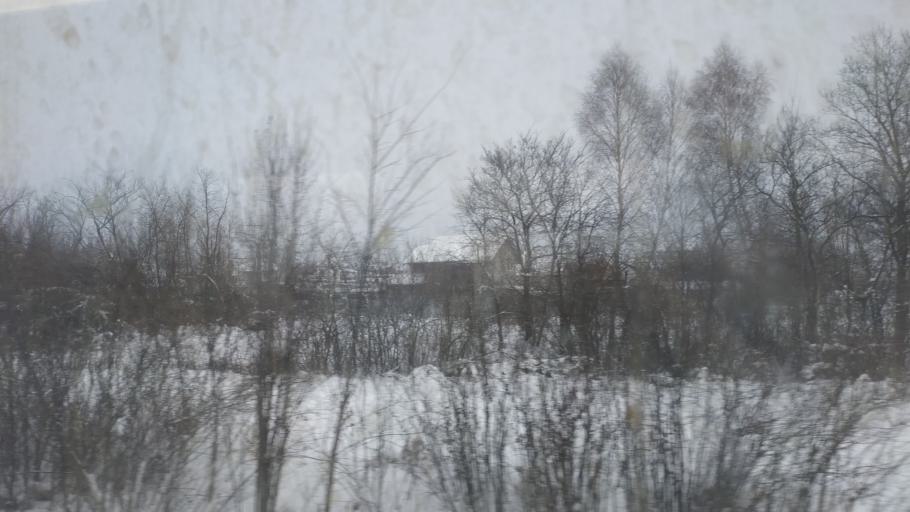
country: RU
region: Moskovskaya
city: Malyshevo
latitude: 55.5261
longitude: 38.3205
